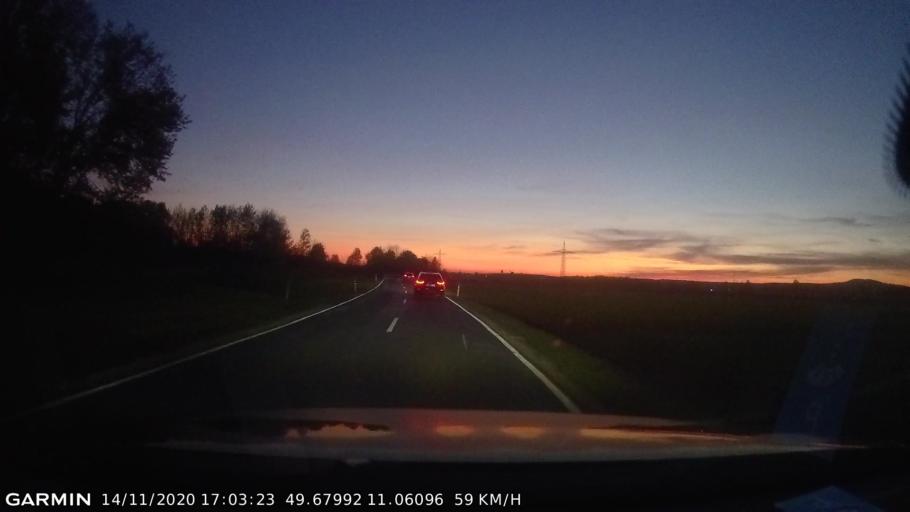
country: DE
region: Bavaria
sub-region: Upper Franconia
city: Poxdorf
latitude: 49.6799
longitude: 11.0610
